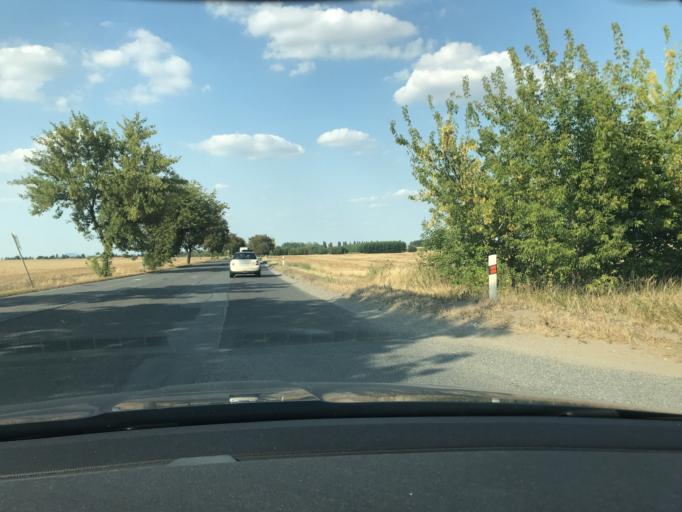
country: CZ
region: Central Bohemia
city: Velke Prilepy
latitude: 50.1772
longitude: 14.3191
